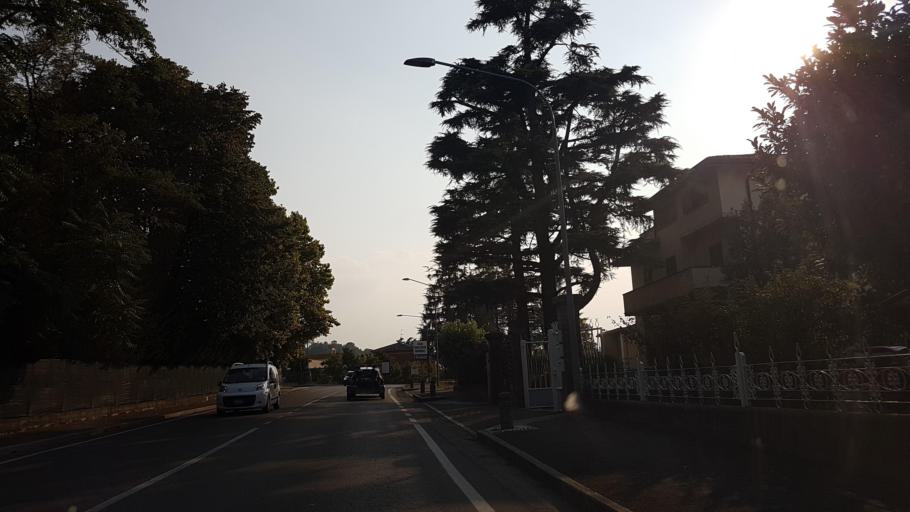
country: IT
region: Emilia-Romagna
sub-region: Provincia di Parma
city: Ozzano Taro
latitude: 44.7100
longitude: 10.1403
